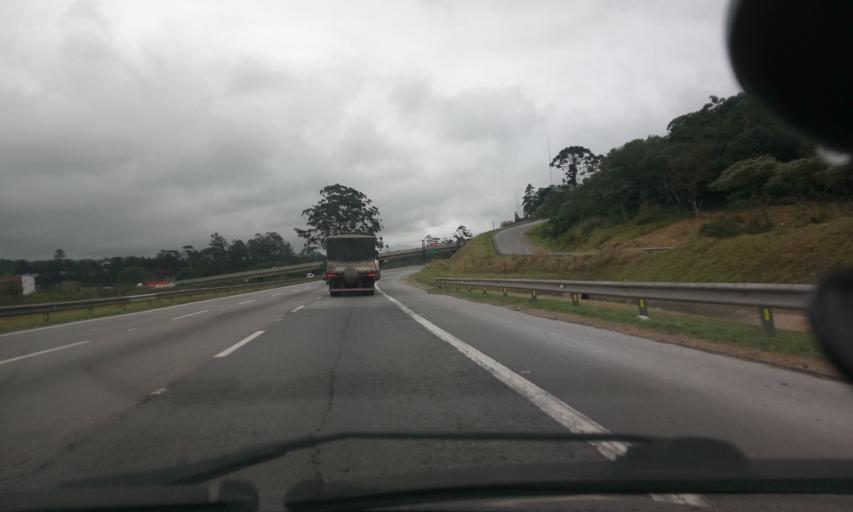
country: BR
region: Sao Paulo
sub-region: Itapecerica Da Serra
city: Itapecerica da Serra
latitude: -23.6953
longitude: -46.8174
